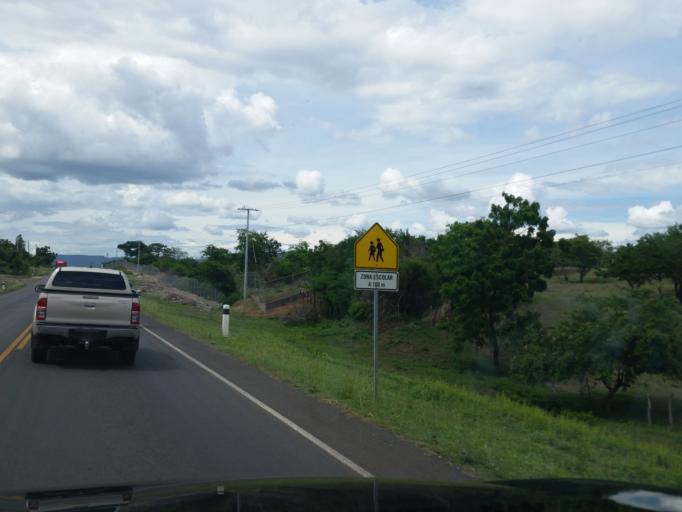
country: NI
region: Managua
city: Tipitapa
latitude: 12.3574
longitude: -86.0486
